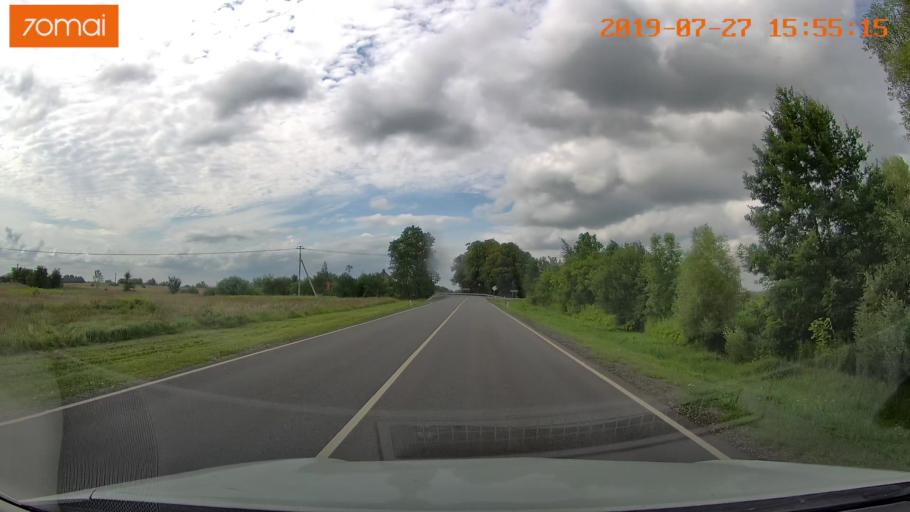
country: RU
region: Kaliningrad
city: Chernyakhovsk
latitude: 54.6128
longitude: 21.9239
